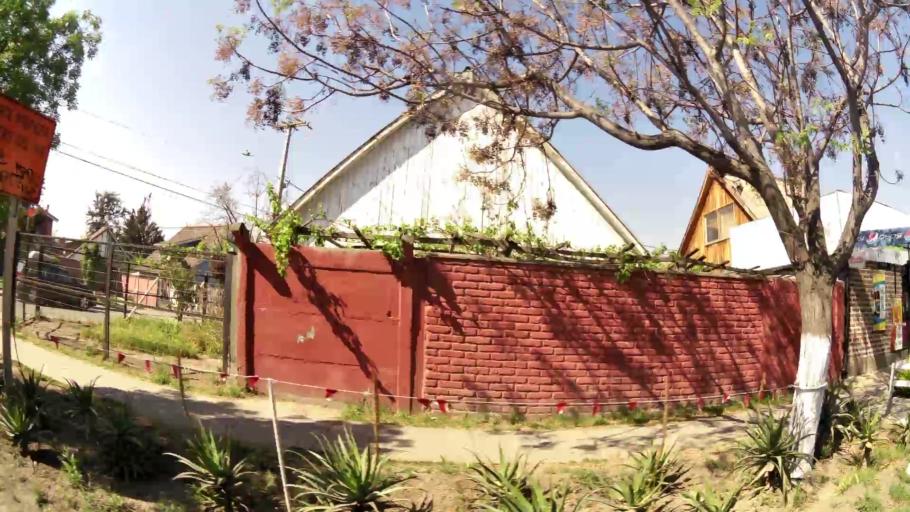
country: CL
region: Santiago Metropolitan
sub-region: Provincia de Santiago
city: La Pintana
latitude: -33.5420
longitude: -70.5956
